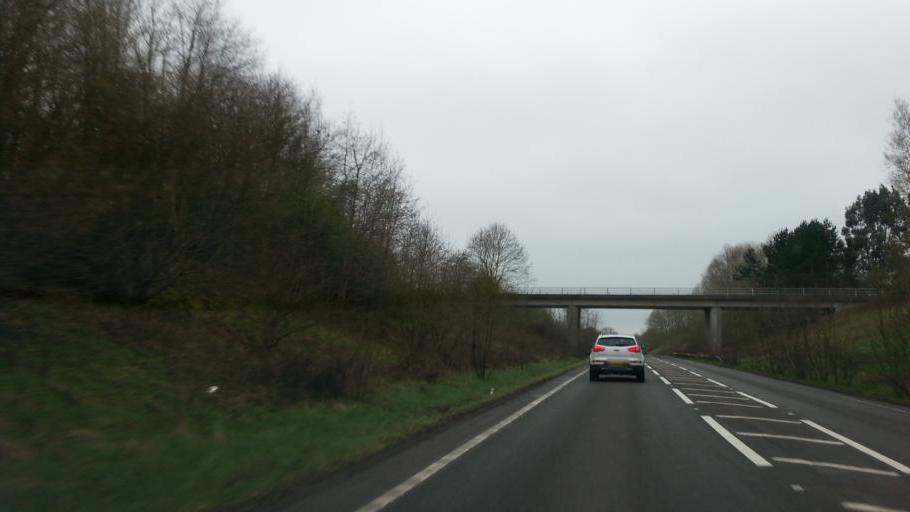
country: GB
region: England
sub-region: Oxfordshire
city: Adderbury
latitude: 52.0688
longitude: -1.2723
